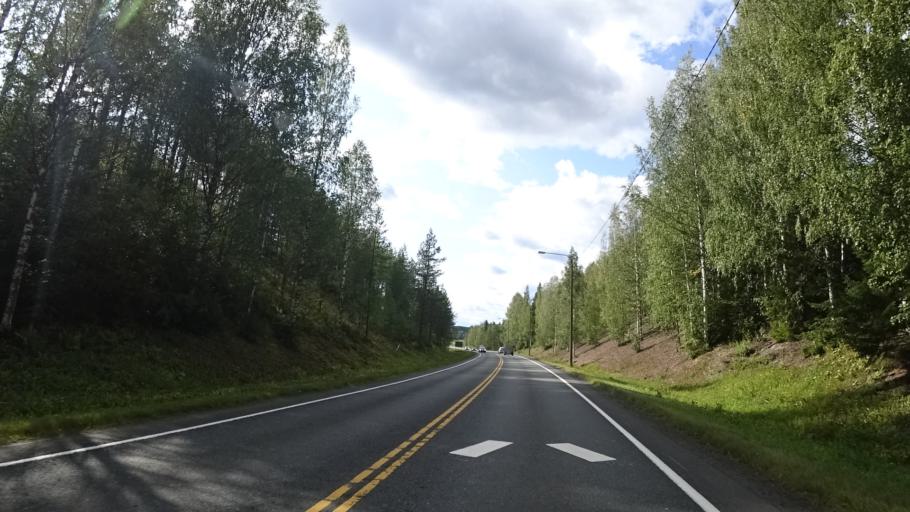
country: FI
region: North Karelia
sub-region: Keski-Karjala
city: Tohmajaervi
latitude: 62.2199
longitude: 30.4036
